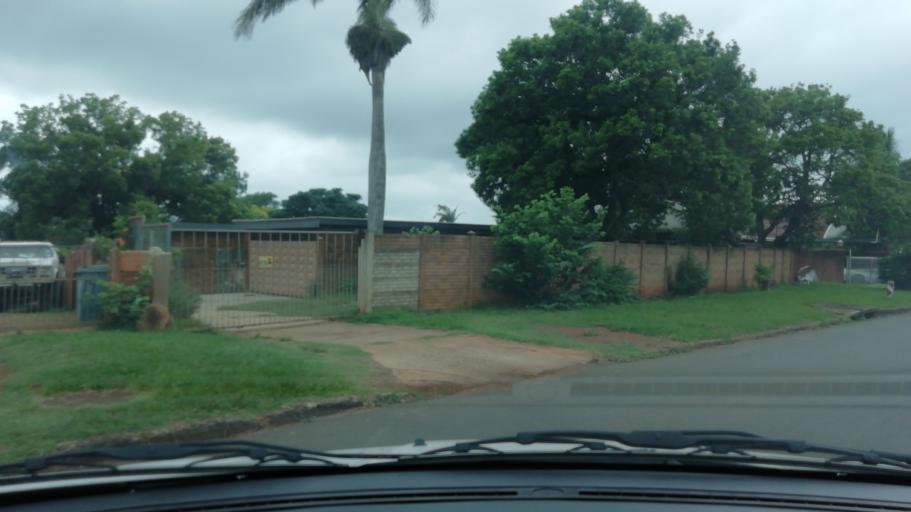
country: ZA
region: KwaZulu-Natal
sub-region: uThungulu District Municipality
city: Empangeni
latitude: -28.7651
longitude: 31.8977
